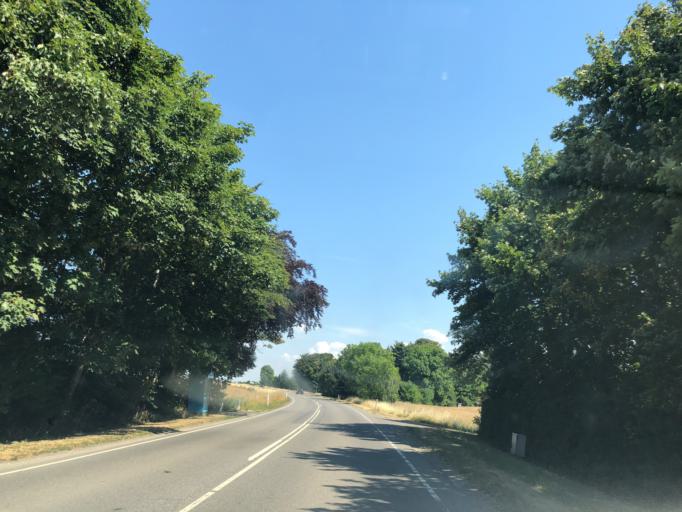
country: DK
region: Zealand
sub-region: Naestved Kommune
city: Fuglebjerg
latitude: 55.2954
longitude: 11.4479
